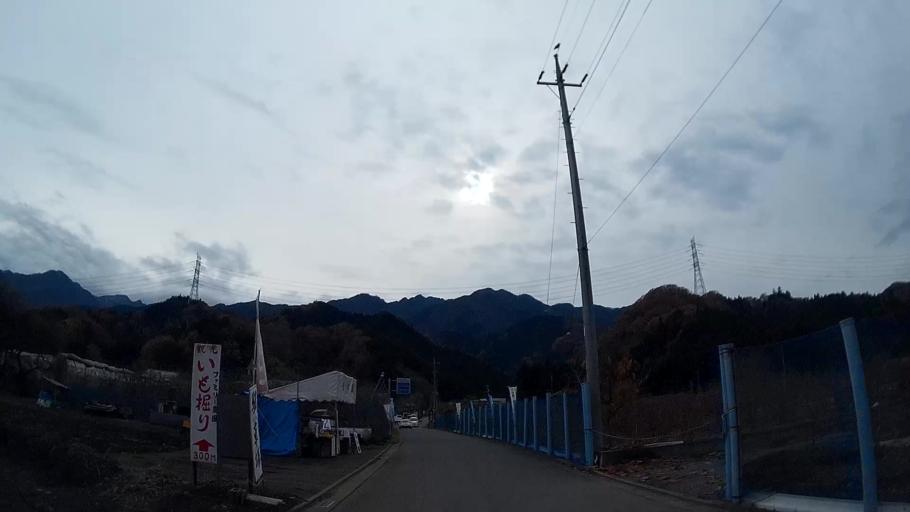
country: JP
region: Saitama
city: Chichibu
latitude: 35.9554
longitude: 139.0128
